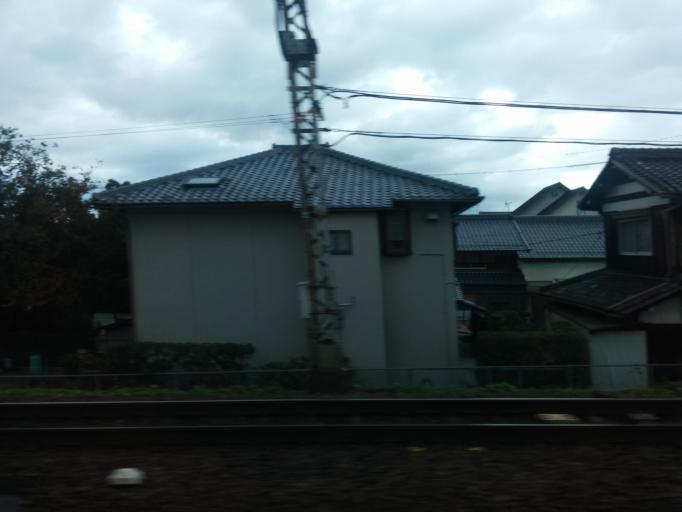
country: JP
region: Shiga Prefecture
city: Kusatsu
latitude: 35.0148
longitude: 135.9556
